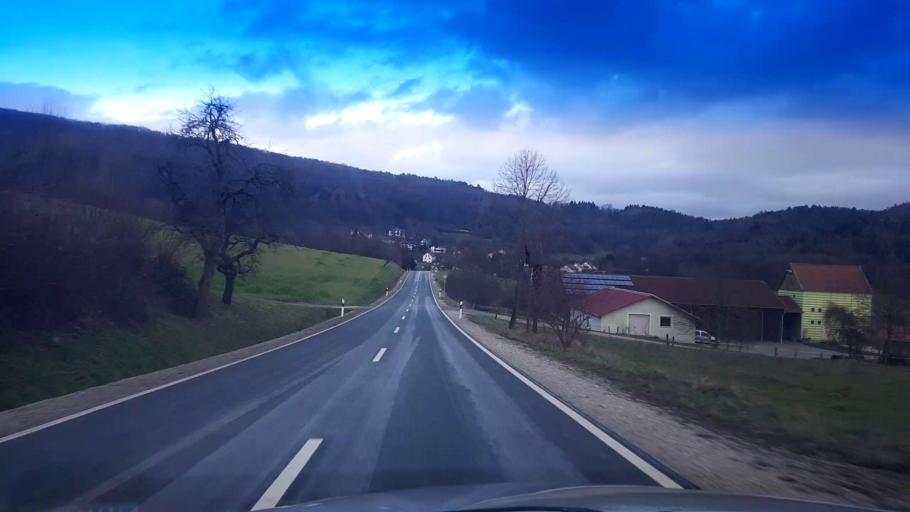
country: DE
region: Bavaria
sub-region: Upper Franconia
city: Buttenheim
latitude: 49.8273
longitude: 11.0521
